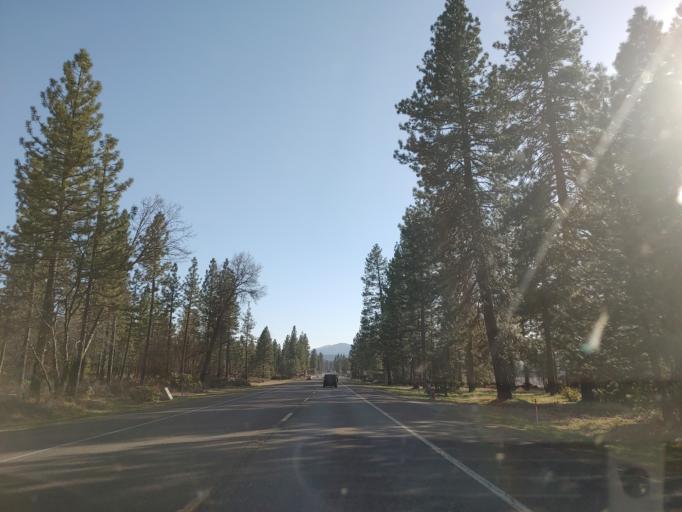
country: US
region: California
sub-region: Shasta County
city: Burney
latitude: 40.8947
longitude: -121.6486
